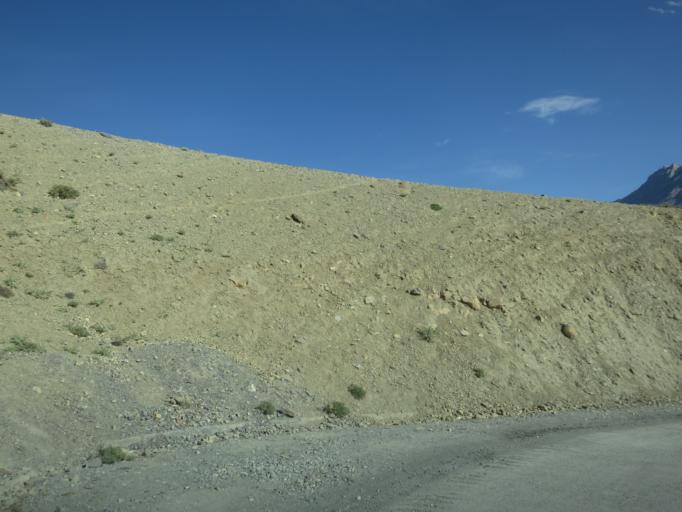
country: IN
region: Himachal Pradesh
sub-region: Shimla
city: Sarahan
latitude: 32.2767
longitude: 78.0264
